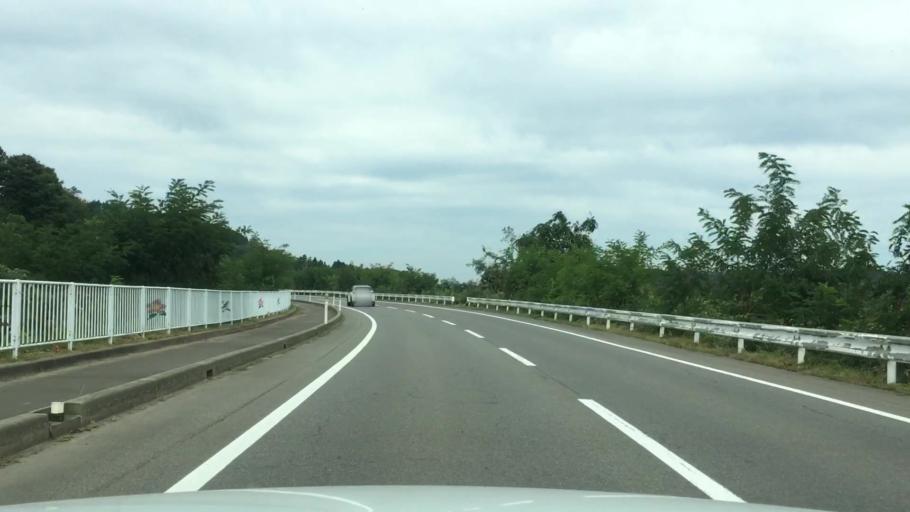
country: JP
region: Aomori
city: Shimokizukuri
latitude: 40.7593
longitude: 140.2297
